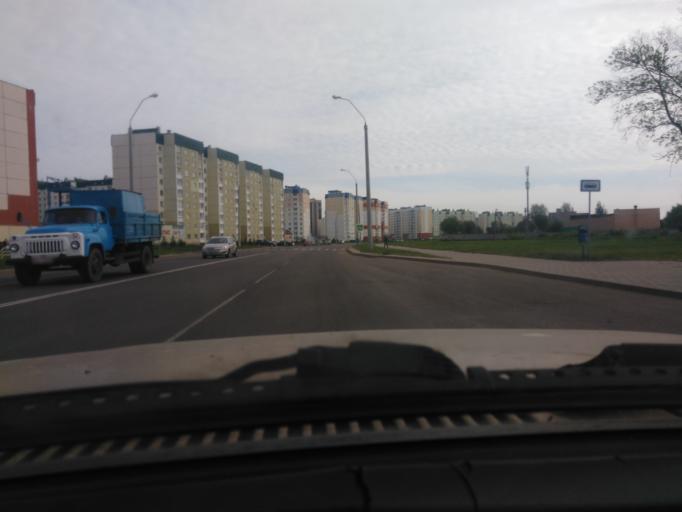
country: BY
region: Mogilev
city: Buynichy
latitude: 53.9118
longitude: 30.2843
